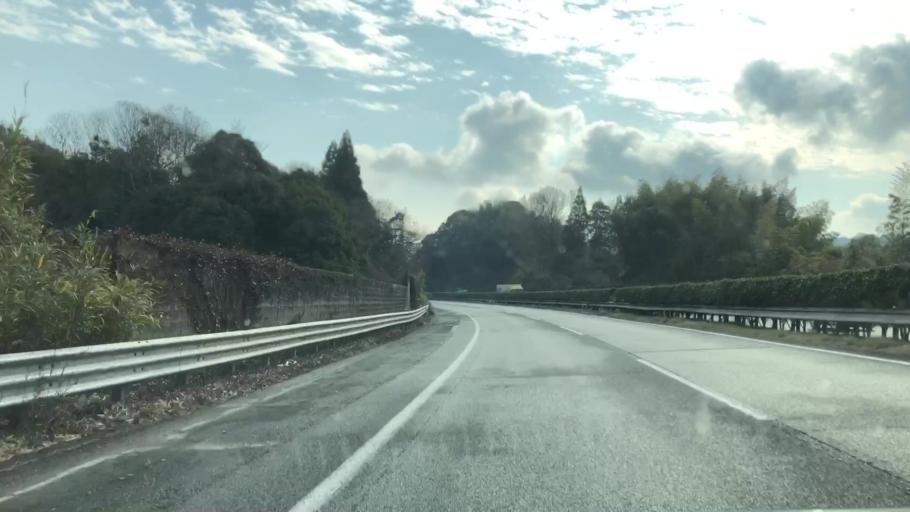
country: JP
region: Kumamoto
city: Tamana
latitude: 33.0076
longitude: 130.5828
